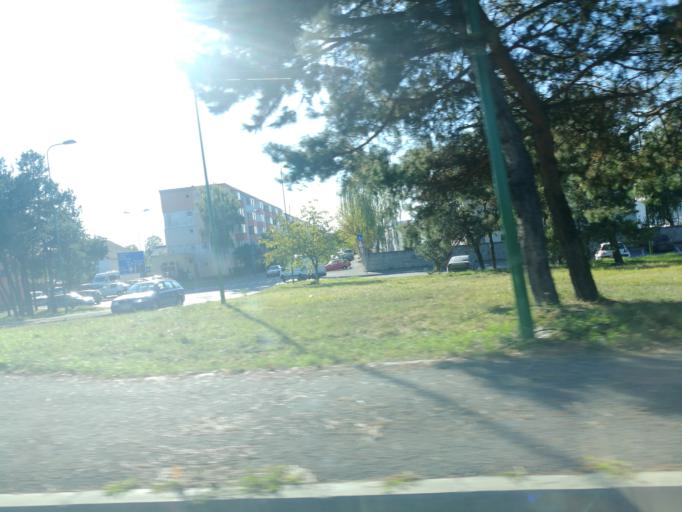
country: RO
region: Brasov
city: Brasov
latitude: 45.6693
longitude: 25.5910
